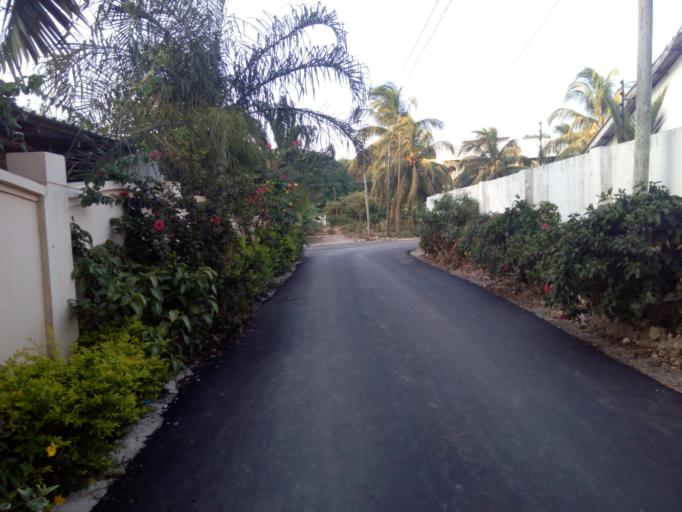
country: TZ
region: Zanzibar Urban/West
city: Zanzibar
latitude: -6.2089
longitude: 39.2025
